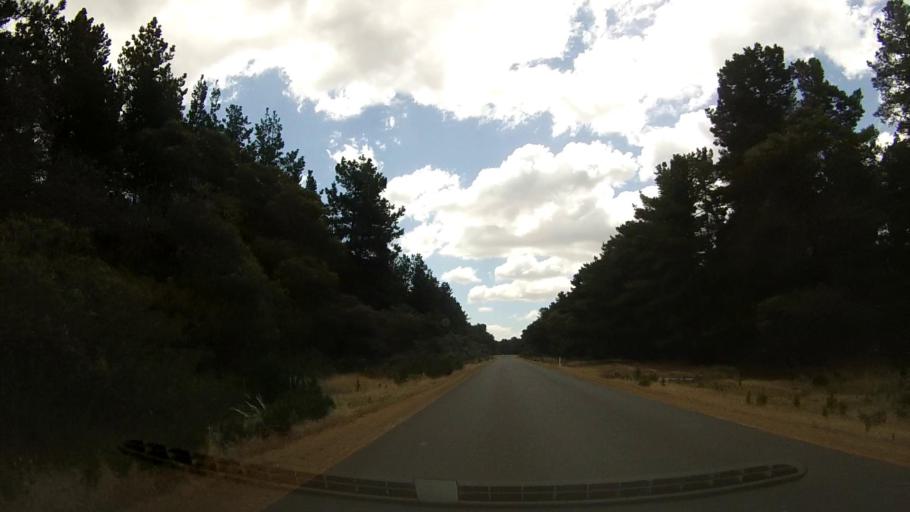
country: AU
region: Tasmania
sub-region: Clarence
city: Seven Mile Beach
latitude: -42.8410
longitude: 147.5316
